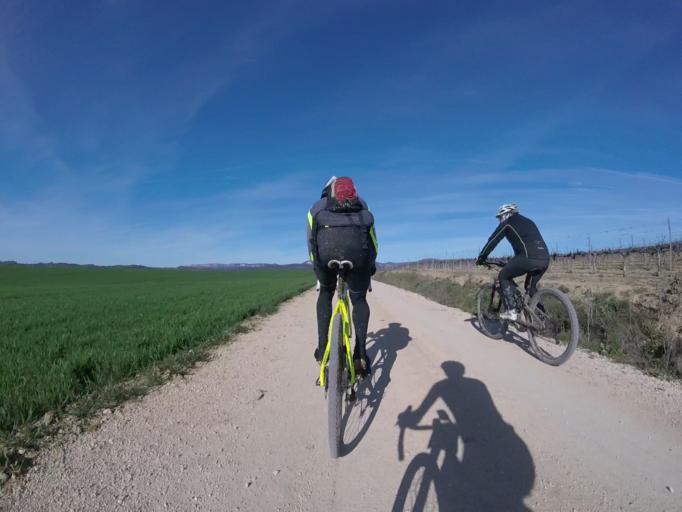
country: ES
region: Navarre
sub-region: Provincia de Navarra
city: Yerri
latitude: 42.7145
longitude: -1.9753
